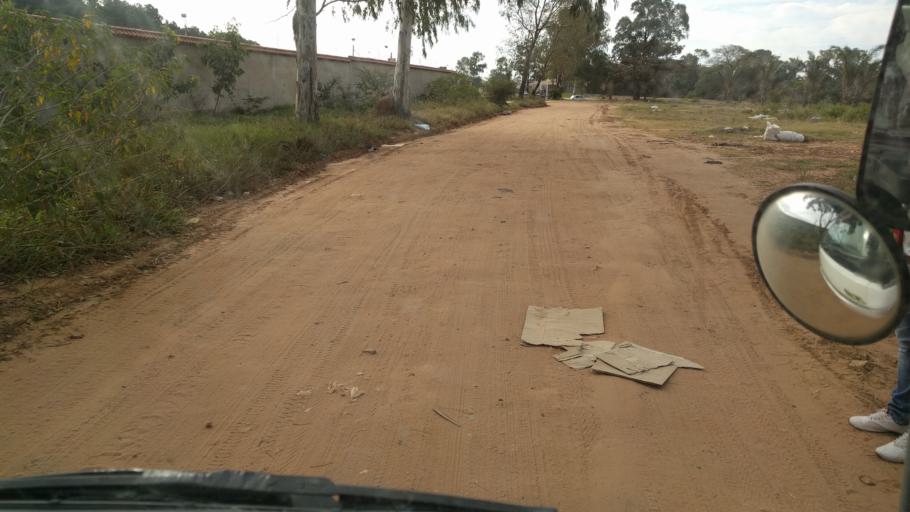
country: BO
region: Santa Cruz
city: Santa Cruz de la Sierra
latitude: -17.6809
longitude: -63.1427
